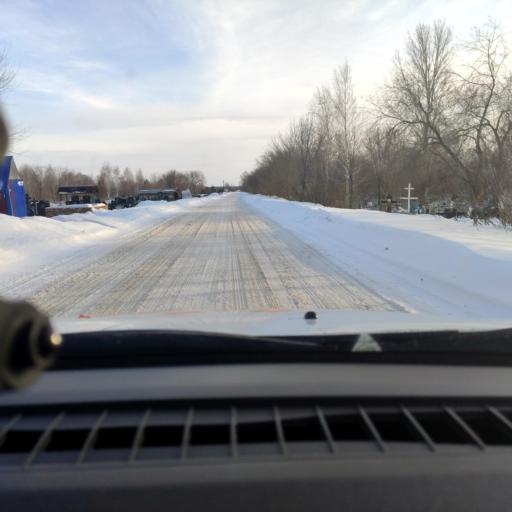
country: RU
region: Samara
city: Chapayevsk
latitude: 52.9915
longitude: 49.7431
